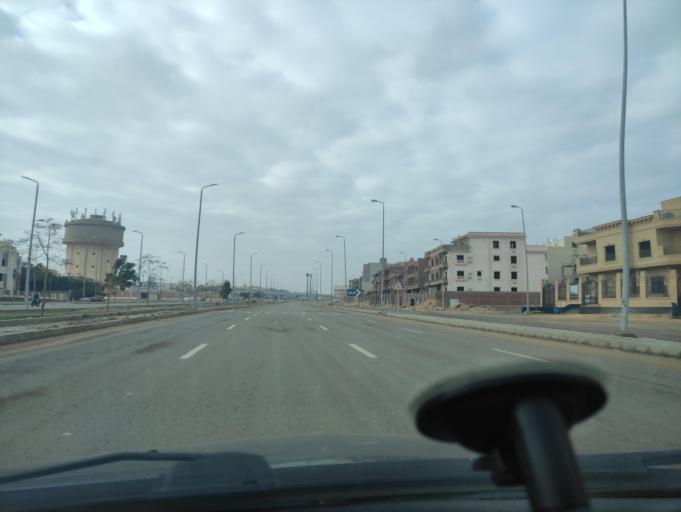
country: EG
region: Muhafazat al Qalyubiyah
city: Al Khankah
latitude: 30.0480
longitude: 31.5285
